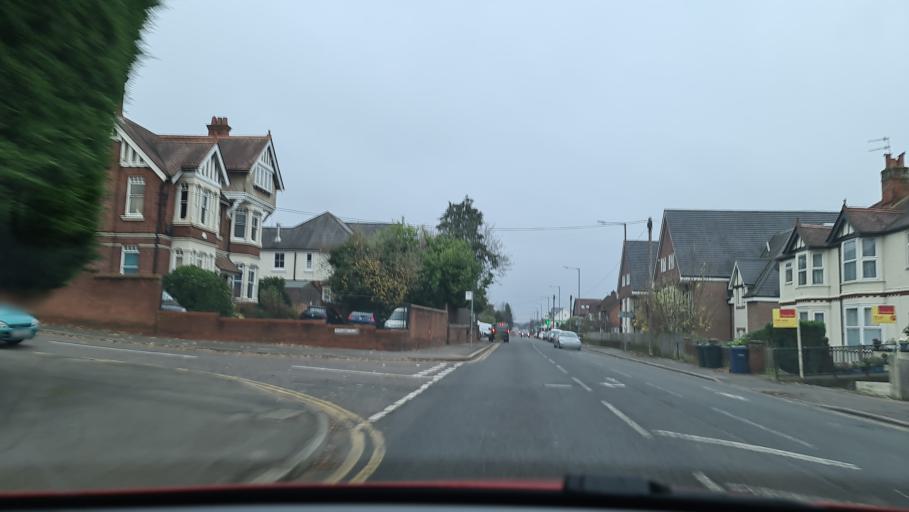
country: GB
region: England
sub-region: Buckinghamshire
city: High Wycombe
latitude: 51.6370
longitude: -0.7712
